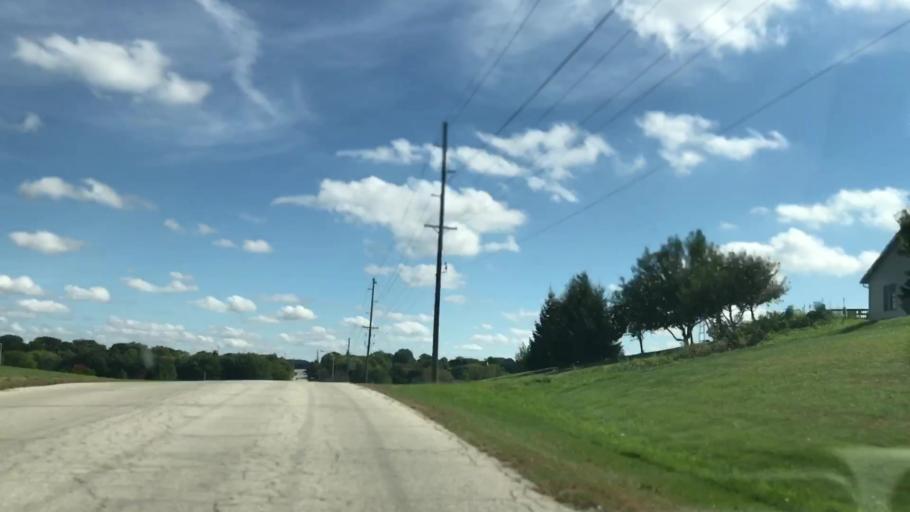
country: US
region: Wisconsin
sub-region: Dodge County
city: Mayville
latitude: 43.5014
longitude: -88.5654
